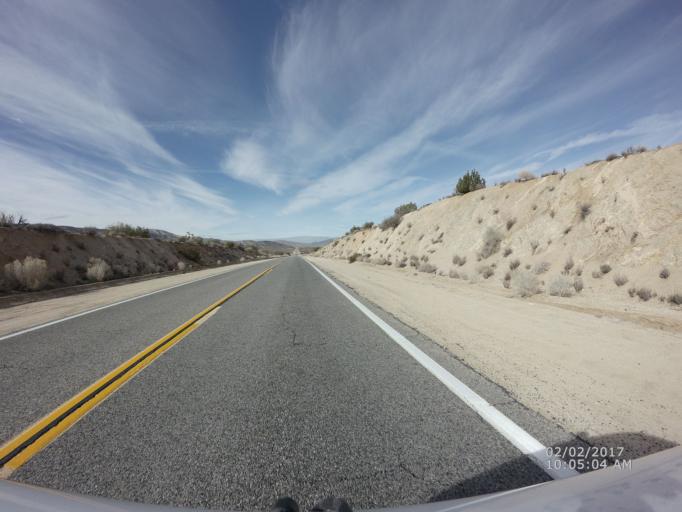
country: US
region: California
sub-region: Los Angeles County
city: Littlerock
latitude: 34.5066
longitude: -117.9835
